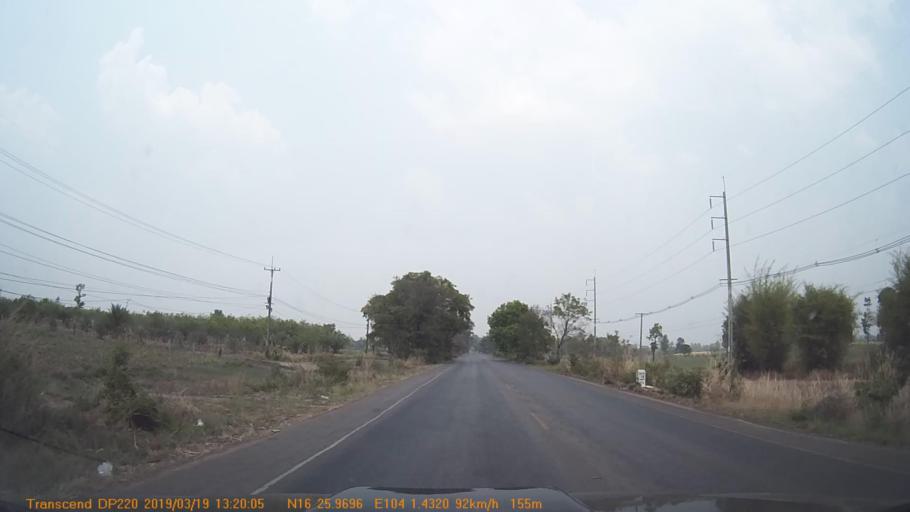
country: TH
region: Kalasin
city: Kuchinarai
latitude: 16.4333
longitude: 104.0240
